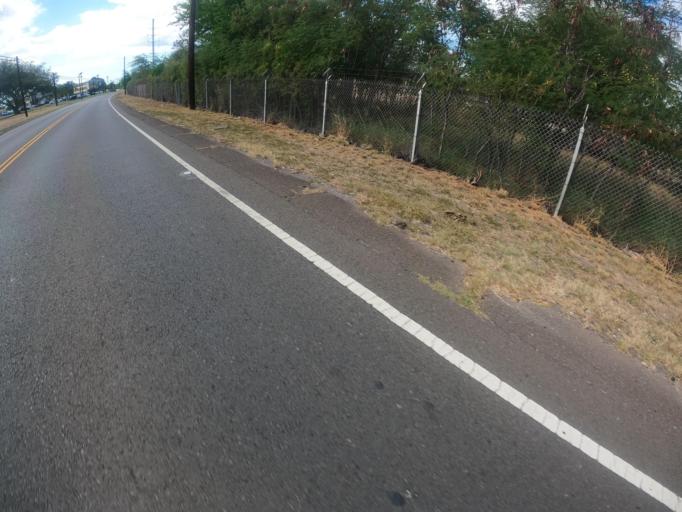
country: US
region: Hawaii
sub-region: Honolulu County
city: Makakilo City
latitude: 21.3228
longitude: -158.0752
